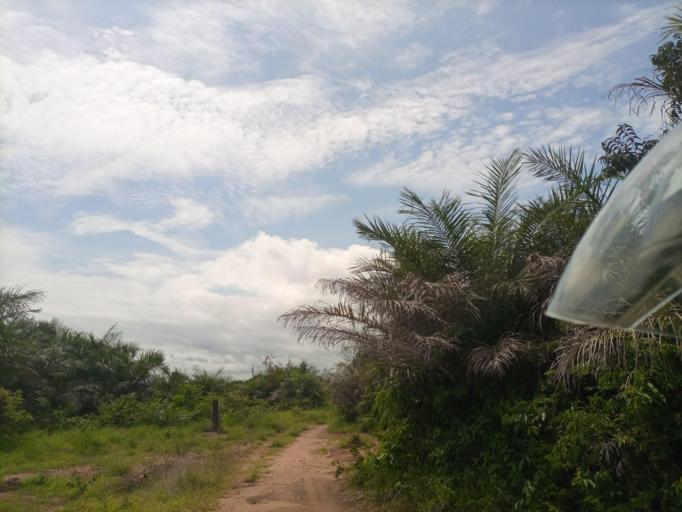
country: SL
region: Northern Province
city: Masoyila
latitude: 8.5422
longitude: -13.1476
